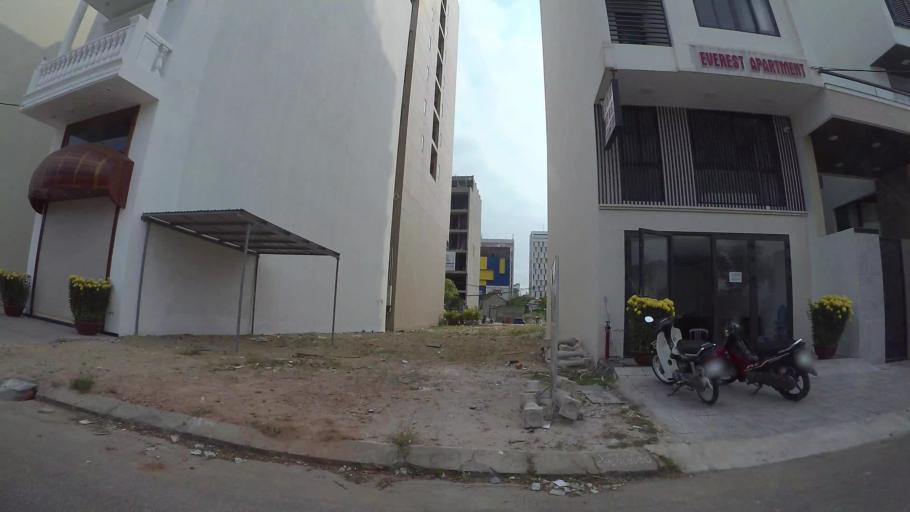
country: VN
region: Da Nang
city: Son Tra
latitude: 16.0721
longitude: 108.2378
